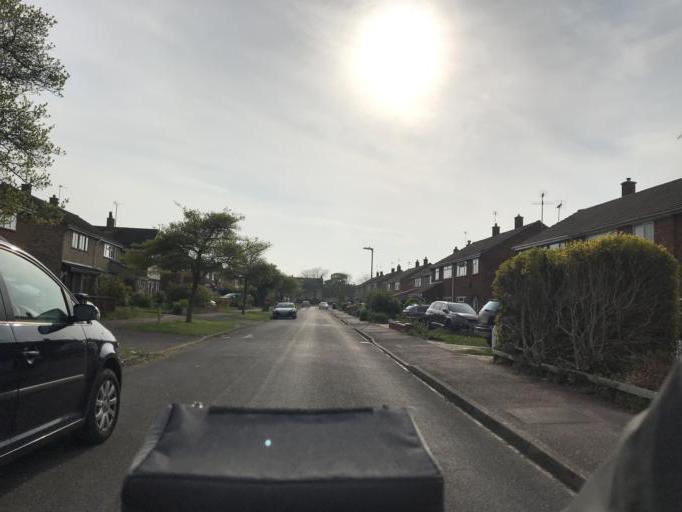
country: GB
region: England
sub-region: Cambridgeshire
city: Fulbourn
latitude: 52.1834
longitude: 0.1677
